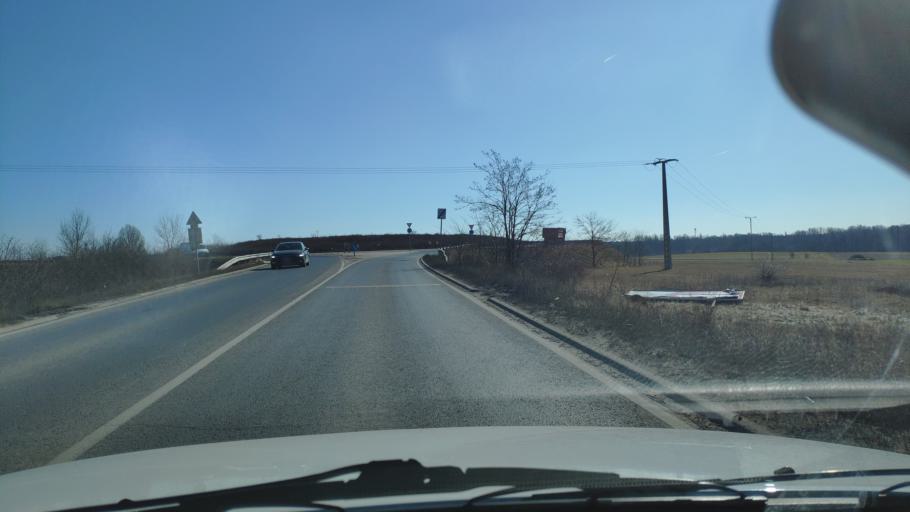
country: HU
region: Pest
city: Kistarcsa
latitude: 47.5185
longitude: 19.2541
